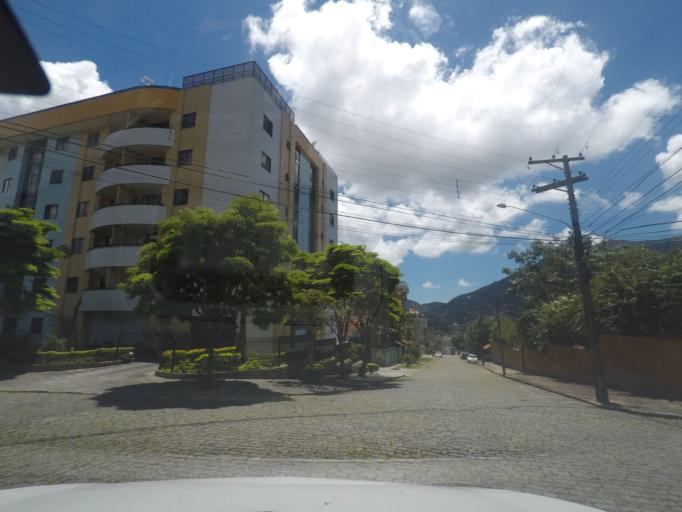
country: BR
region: Rio de Janeiro
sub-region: Teresopolis
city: Teresopolis
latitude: -22.4331
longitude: -42.9821
